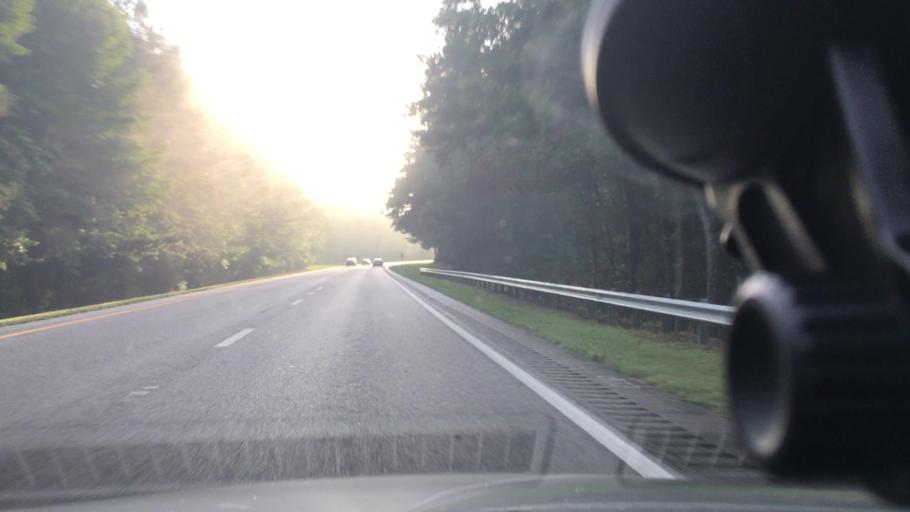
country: US
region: North Carolina
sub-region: Wake County
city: Zebulon
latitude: 35.7948
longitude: -78.1601
